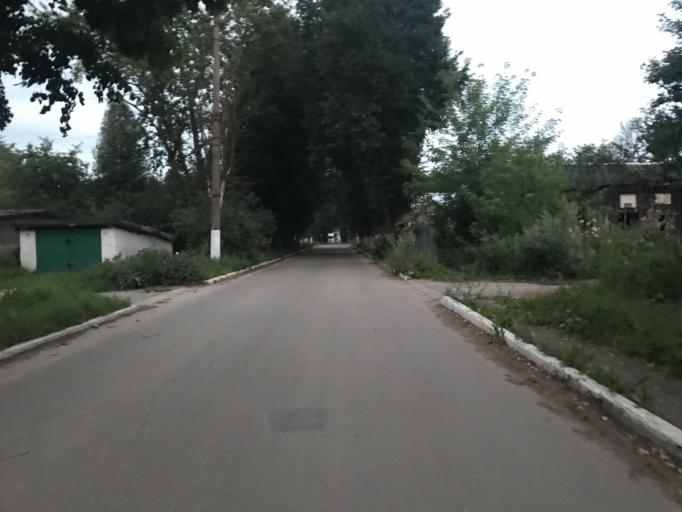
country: RU
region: Tula
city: Priupskiy
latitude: 53.9389
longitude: 37.6992
